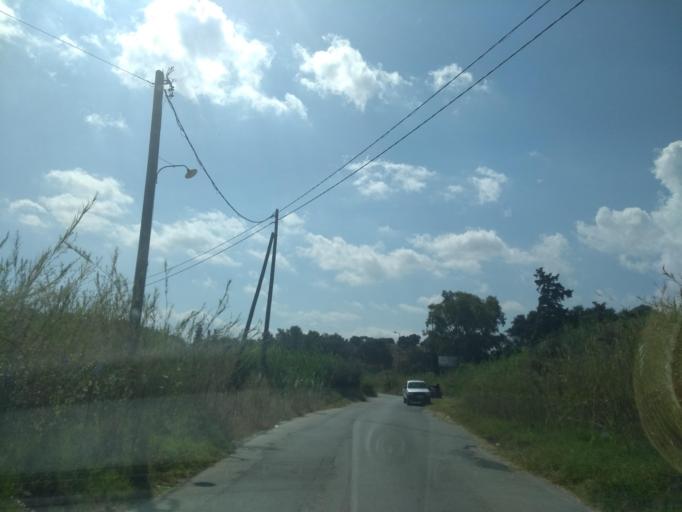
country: GR
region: Crete
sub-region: Nomos Chanias
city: Georgioupolis
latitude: 35.3583
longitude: 24.2631
